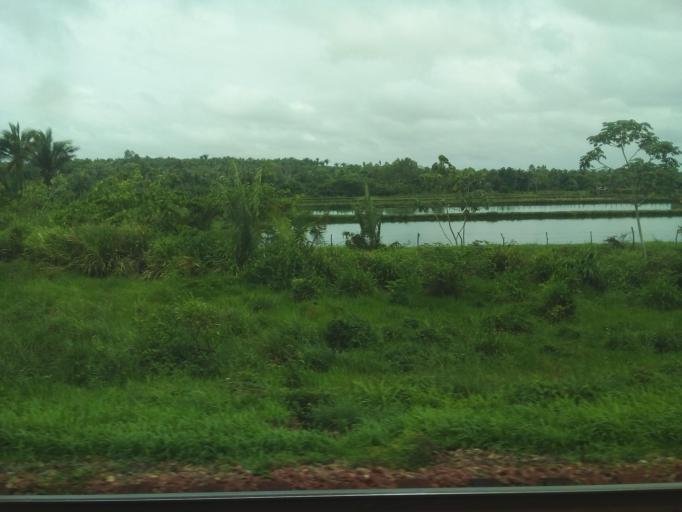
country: BR
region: Maranhao
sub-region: Vitoria Do Mearim
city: Vitoria do Mearim
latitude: -3.5421
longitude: -44.8893
